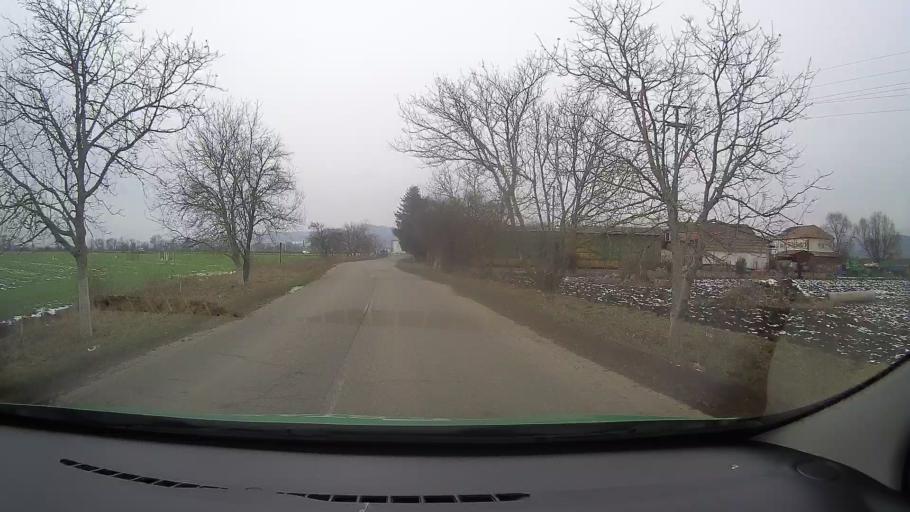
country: RO
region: Hunedoara
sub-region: Comuna Romos
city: Romos
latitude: 45.8829
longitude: 23.2520
